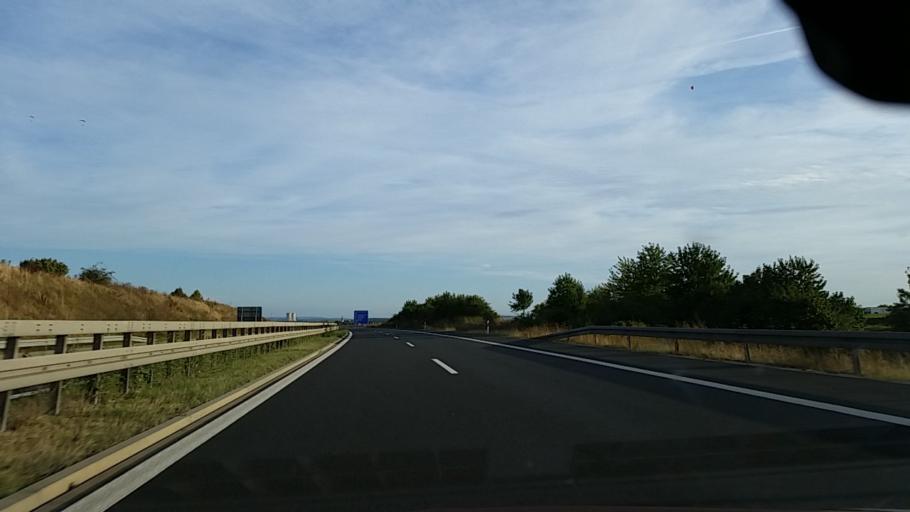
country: DE
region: Bavaria
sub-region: Regierungsbezirk Unterfranken
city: Euerbach
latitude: 50.0688
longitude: 10.1467
